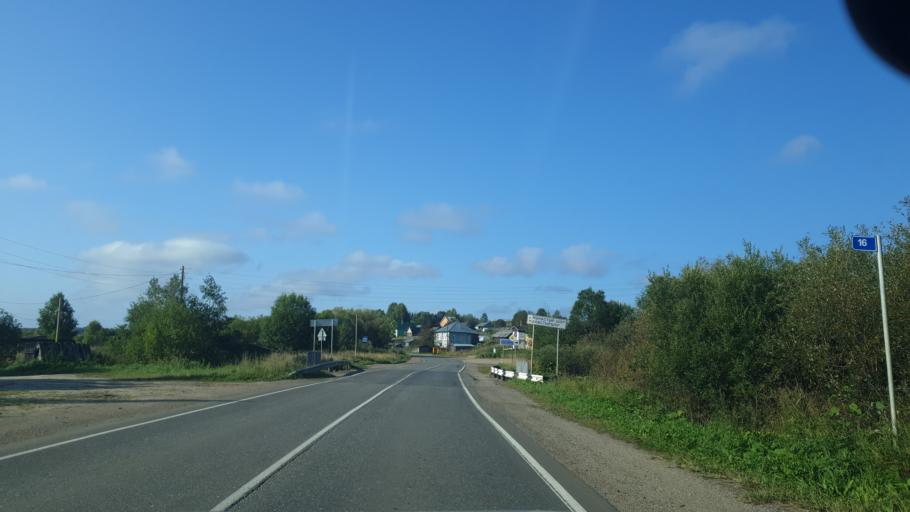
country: RU
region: Komi Republic
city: Vizinga
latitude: 60.9682
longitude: 50.2468
